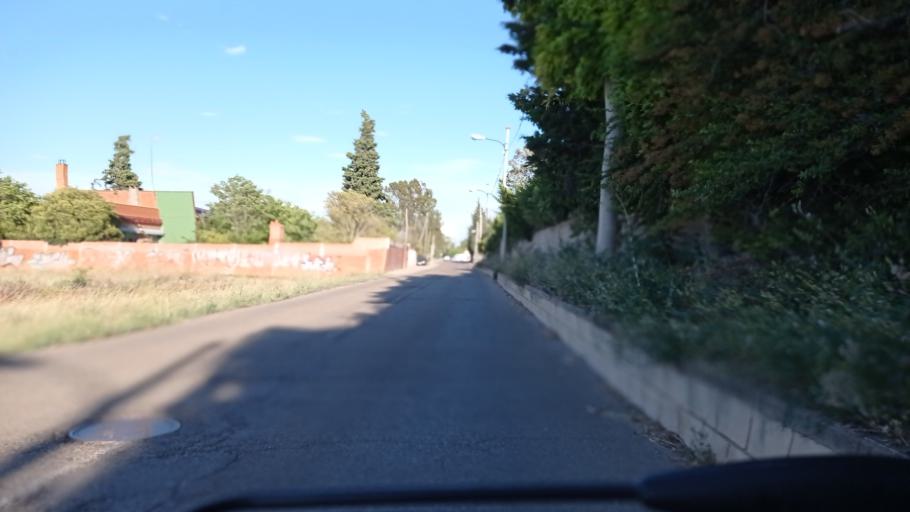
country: ES
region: Aragon
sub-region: Provincia de Zaragoza
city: Oliver-Valdefierro, Oliver, Valdefierro
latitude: 41.6734
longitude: -0.9542
